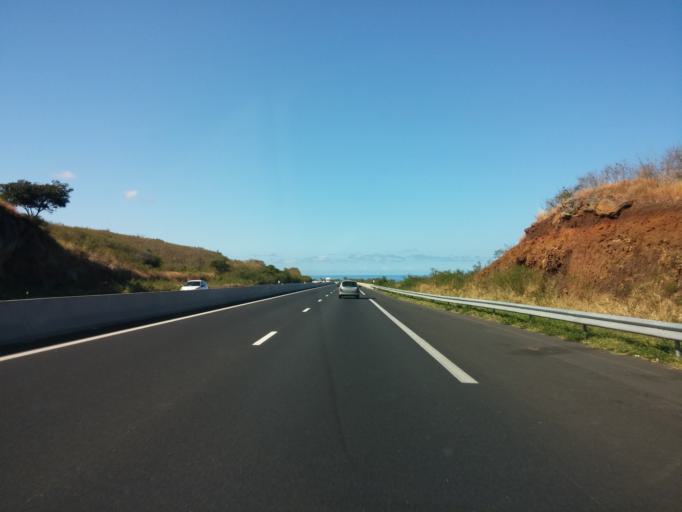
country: RE
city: Piton Saint-Leu
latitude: -21.2371
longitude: 55.3141
